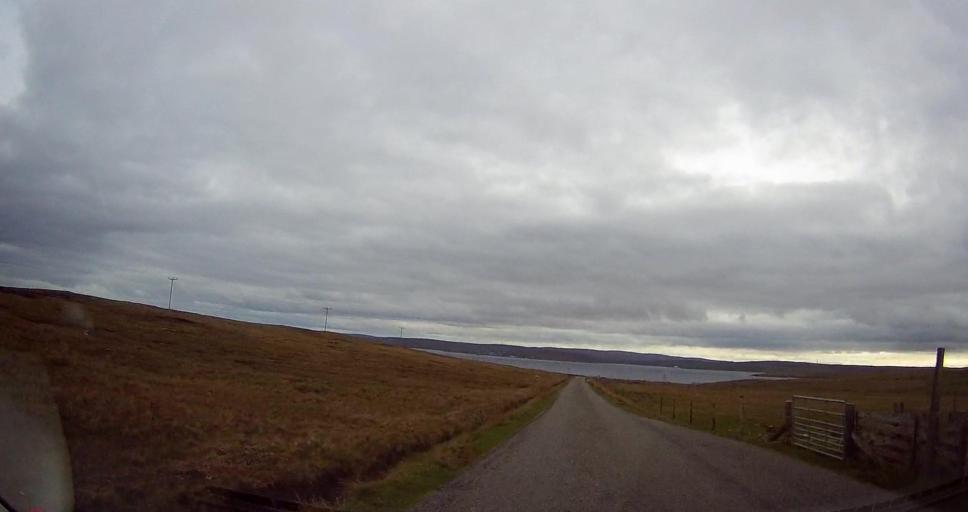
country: GB
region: Scotland
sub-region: Shetland Islands
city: Shetland
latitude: 60.5044
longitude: -1.1467
